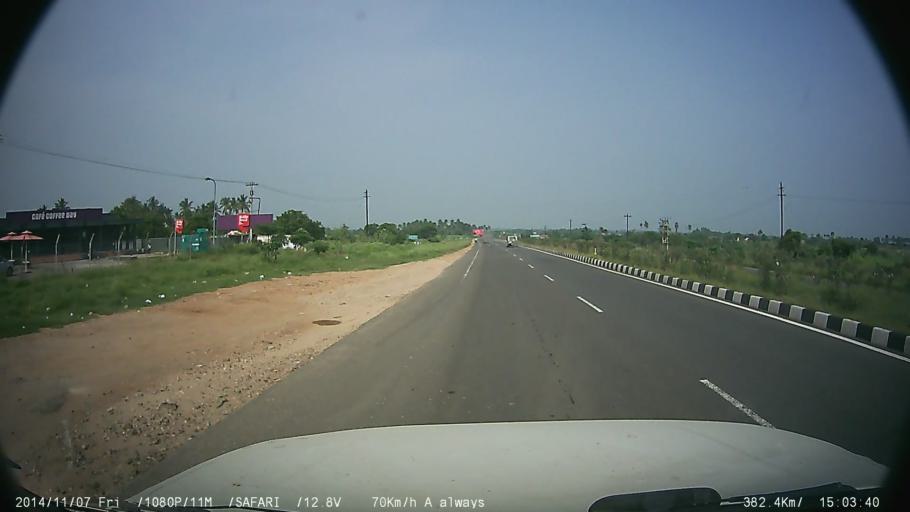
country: IN
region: Tamil Nadu
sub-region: Tiruppur
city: Uttukkuli
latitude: 11.2128
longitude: 77.4421
